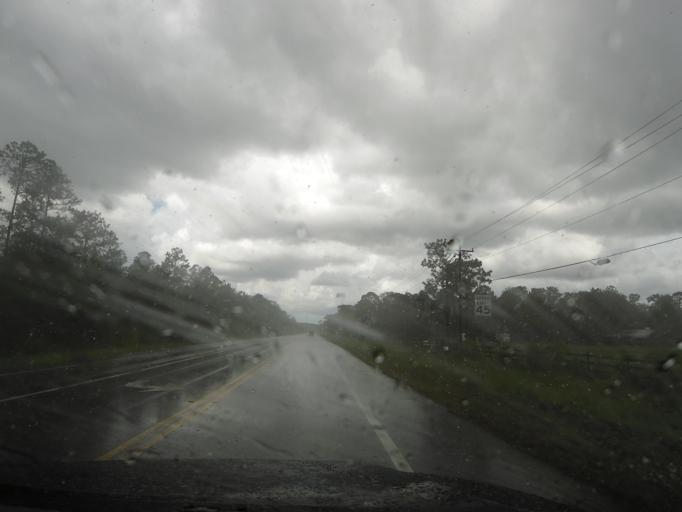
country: US
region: Florida
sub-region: Clay County
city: Asbury Lake
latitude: 30.0302
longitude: -81.8103
